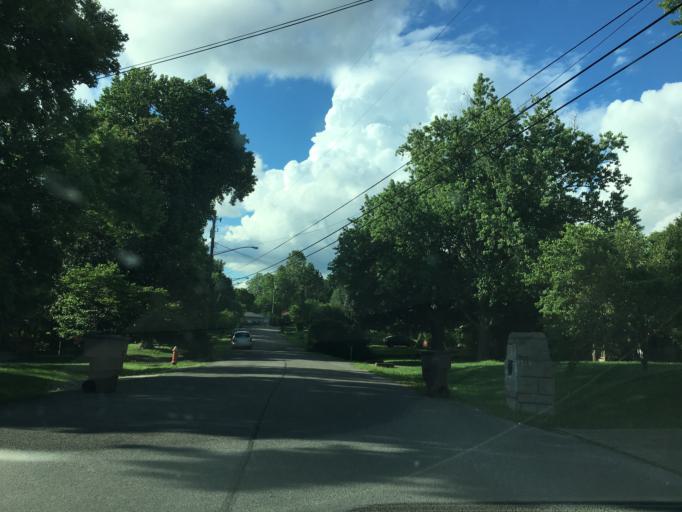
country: US
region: Tennessee
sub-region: Davidson County
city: Oak Hill
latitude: 36.0929
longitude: -86.7330
